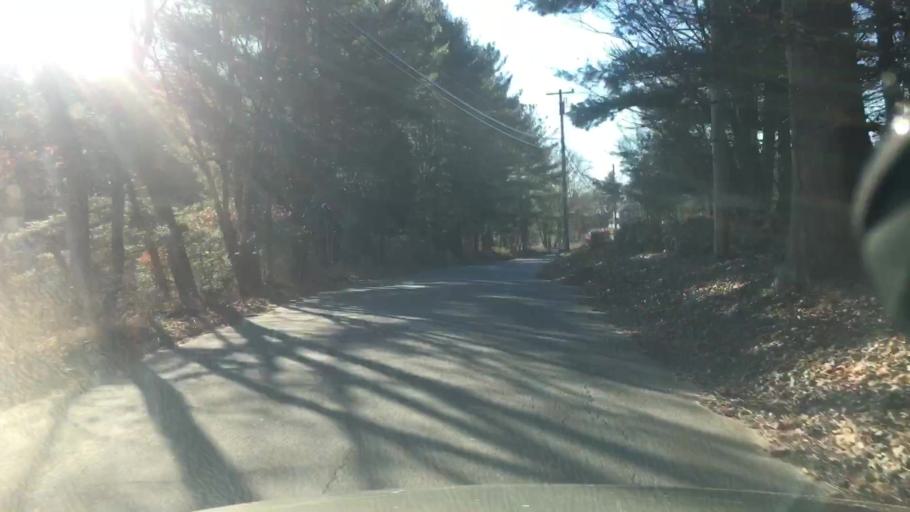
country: US
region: Connecticut
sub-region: Tolland County
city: Stafford
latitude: 41.9798
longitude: -72.2968
